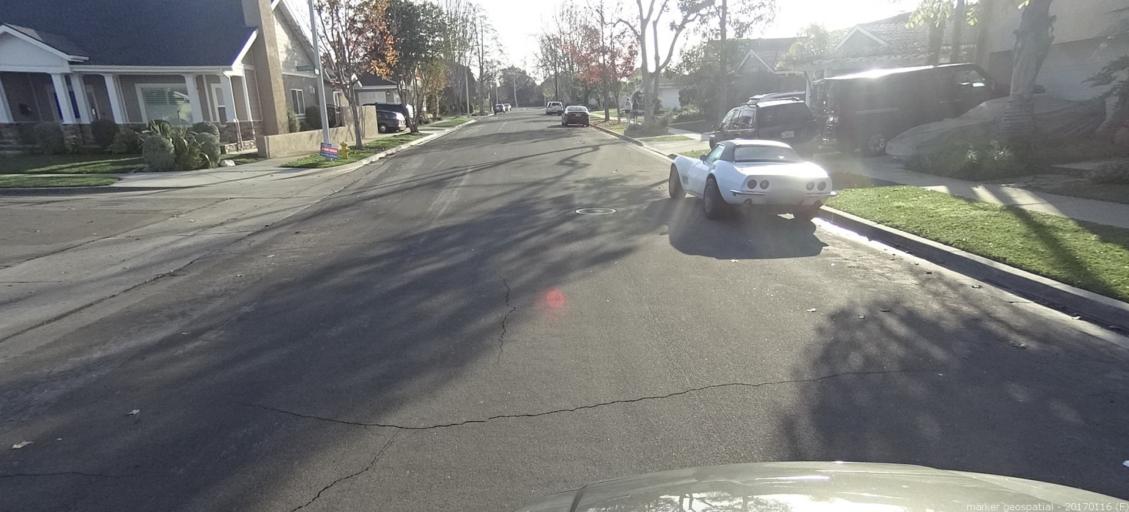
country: US
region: California
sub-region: Orange County
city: Rossmoor
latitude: 33.7945
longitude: -118.0817
